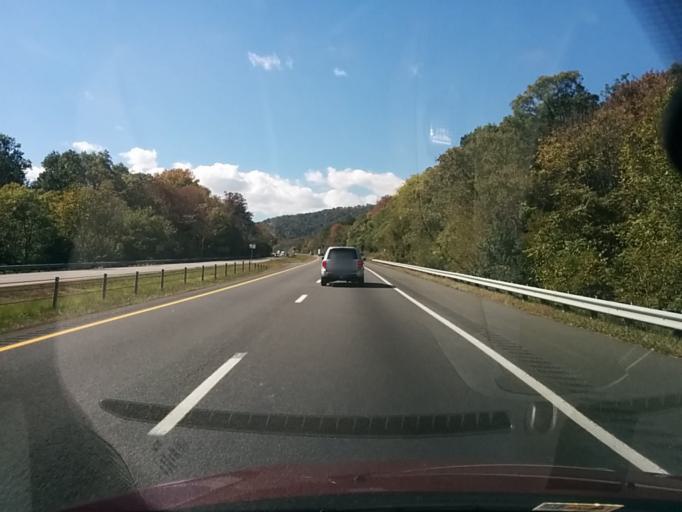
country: US
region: Virginia
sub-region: Albemarle County
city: Crozet
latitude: 38.0475
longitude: -78.7773
